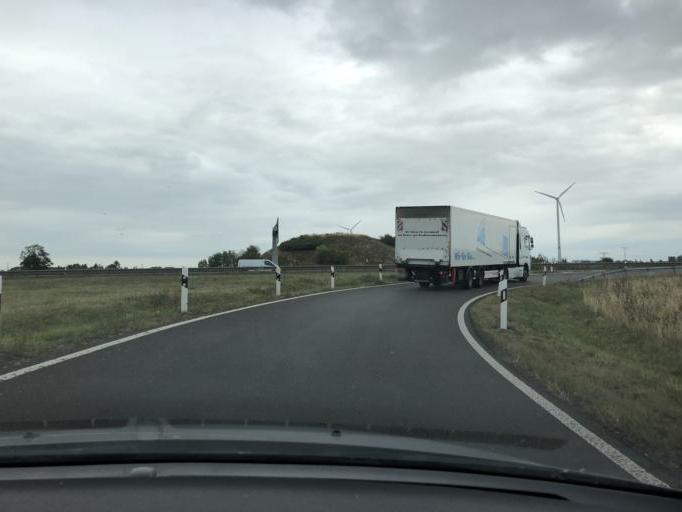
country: DE
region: Saxony
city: Rackwitz
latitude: 51.3971
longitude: 12.4195
